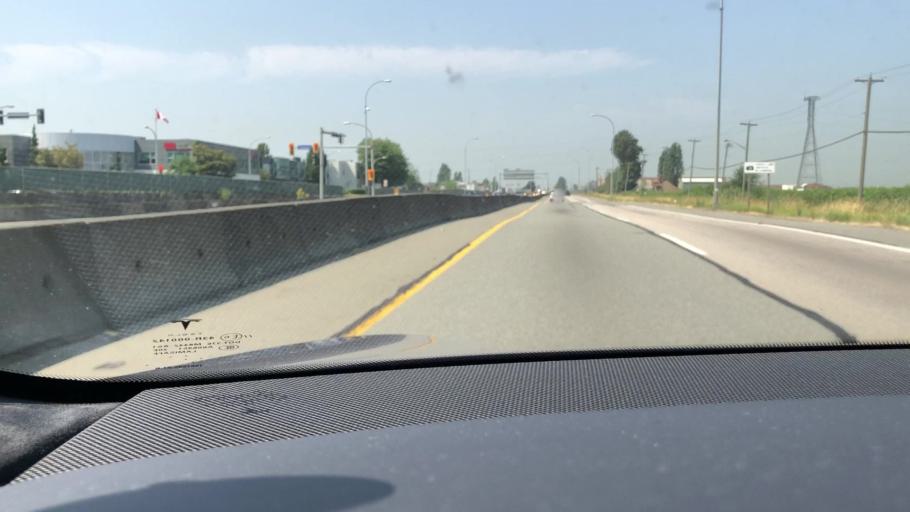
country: CA
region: British Columbia
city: Delta
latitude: 49.1698
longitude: -122.9821
